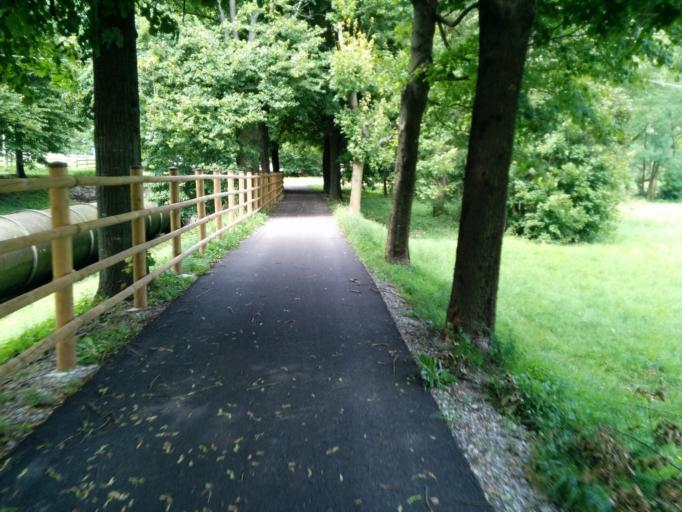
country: IT
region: Friuli Venezia Giulia
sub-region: Provincia di Udine
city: Lauco
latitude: 46.4091
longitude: 12.9478
